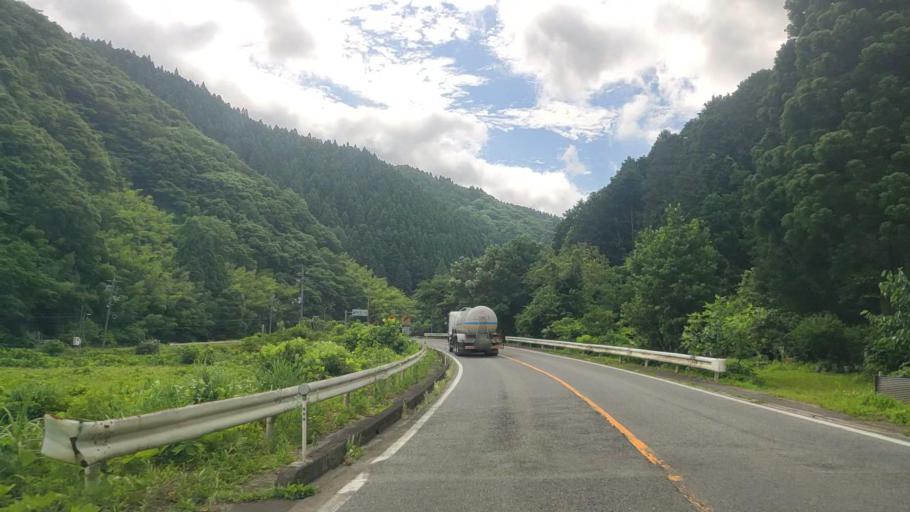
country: JP
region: Tottori
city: Yonago
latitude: 35.2316
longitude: 133.4406
